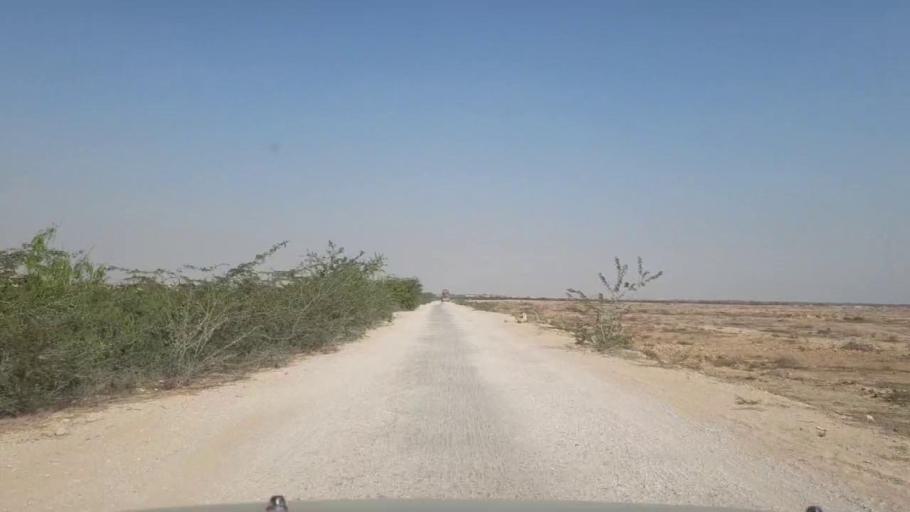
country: PK
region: Sindh
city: Thatta
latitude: 24.9695
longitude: 67.9662
